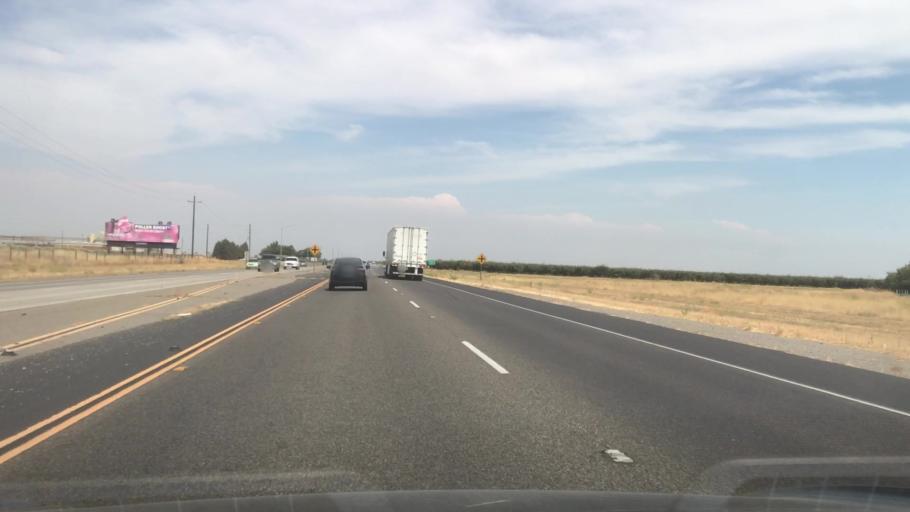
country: US
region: California
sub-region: Madera County
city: Chowchilla
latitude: 37.0837
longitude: -120.2599
